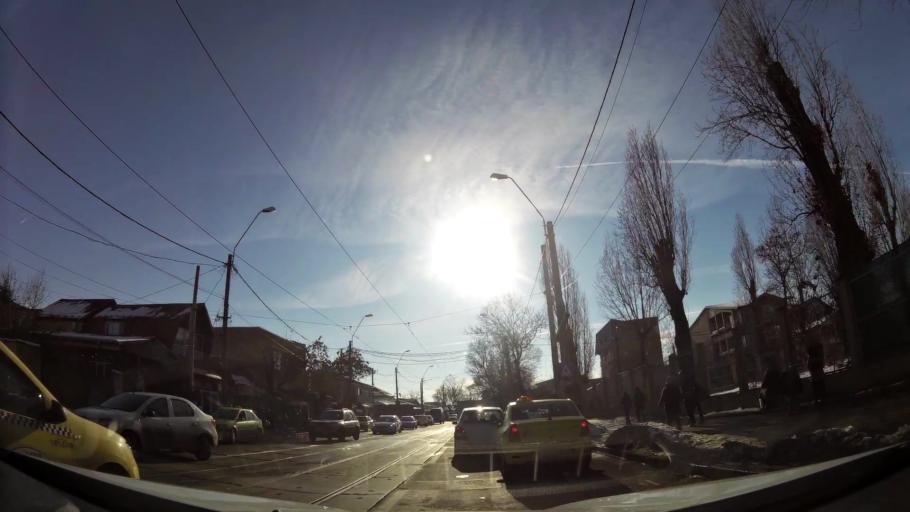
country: RO
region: Bucuresti
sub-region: Municipiul Bucuresti
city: Bucuresti
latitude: 44.3902
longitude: 26.0807
